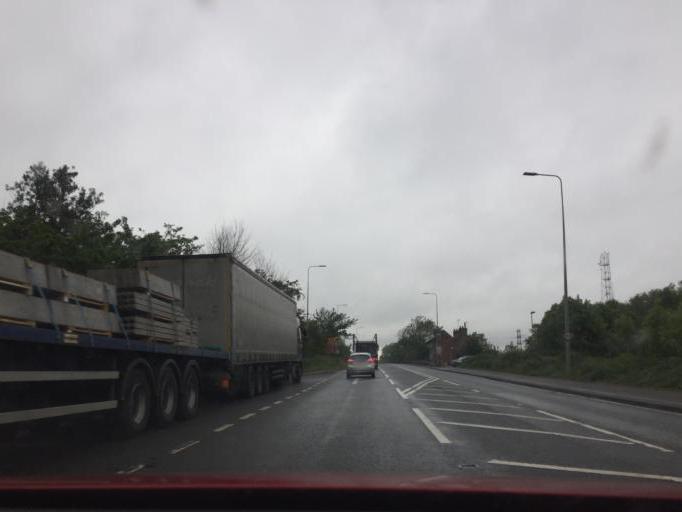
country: GB
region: England
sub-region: Leicestershire
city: Hinckley
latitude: 52.5268
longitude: -1.3926
